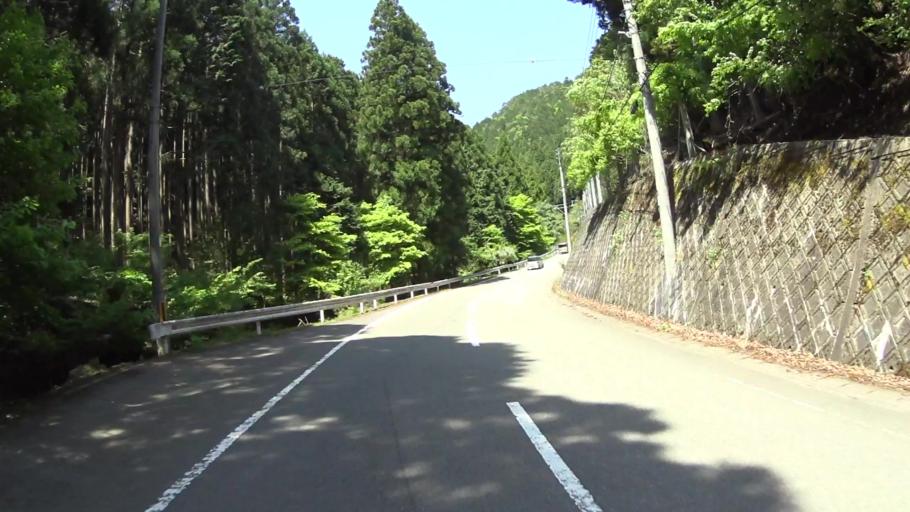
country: JP
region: Shiga Prefecture
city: Kitahama
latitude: 35.1511
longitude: 135.8266
